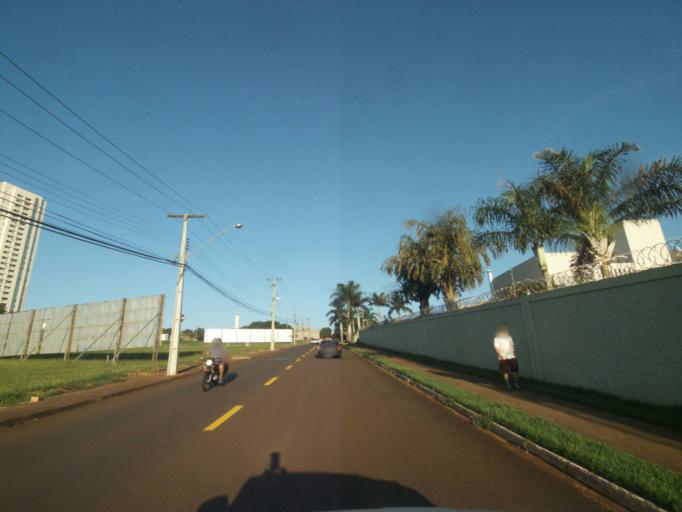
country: BR
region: Parana
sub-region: Londrina
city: Londrina
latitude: -23.3456
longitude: -51.1912
